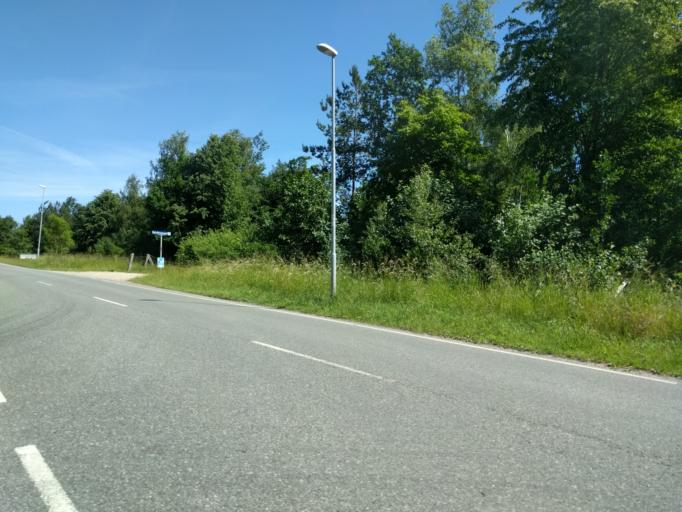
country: DK
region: South Denmark
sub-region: Kerteminde Kommune
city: Langeskov
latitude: 55.3477
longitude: 10.5821
